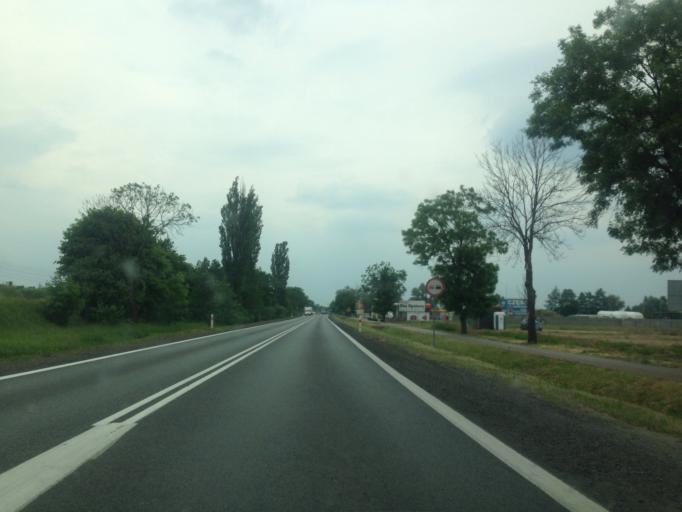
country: PL
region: Kujawsko-Pomorskie
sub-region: Grudziadz
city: Grudziadz
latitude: 53.4890
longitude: 18.7210
